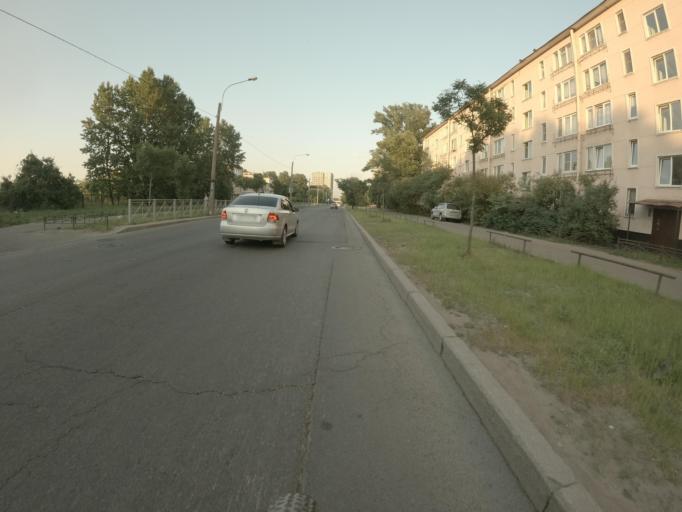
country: RU
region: St.-Petersburg
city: Avtovo
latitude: 59.8543
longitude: 30.2723
